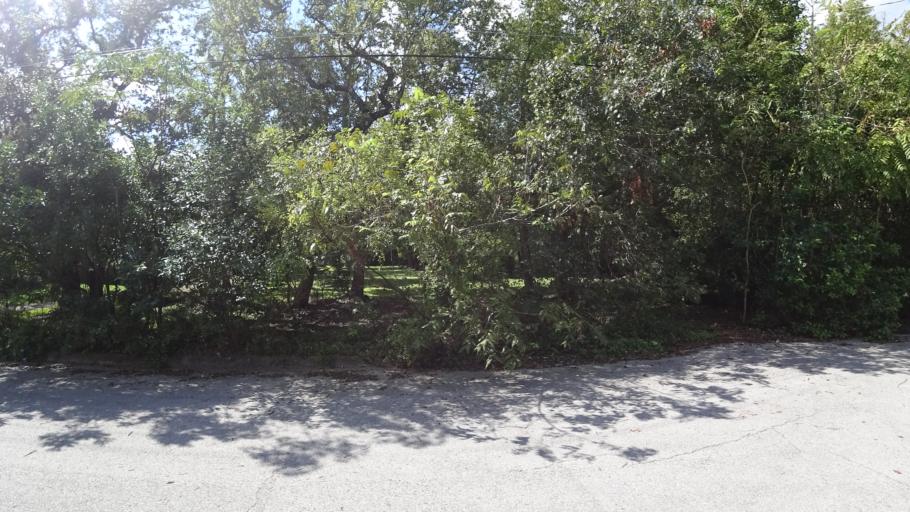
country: US
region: Texas
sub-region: Travis County
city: Manchaca
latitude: 30.1936
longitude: -97.8063
